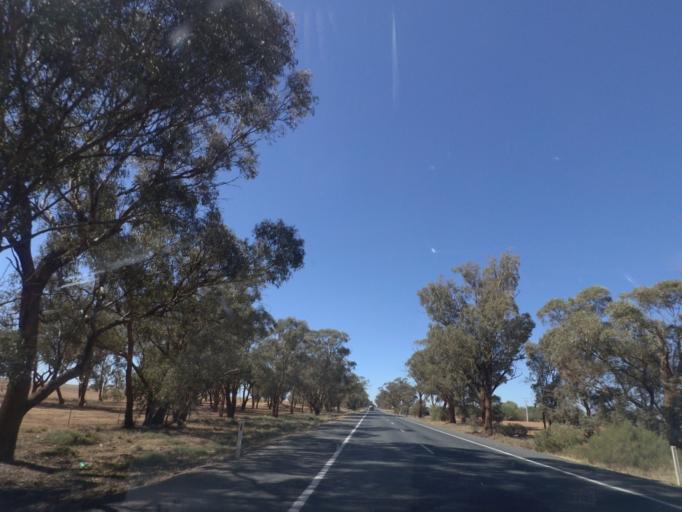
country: AU
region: New South Wales
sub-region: Bland
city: West Wyalong
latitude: -34.2054
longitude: 147.1097
